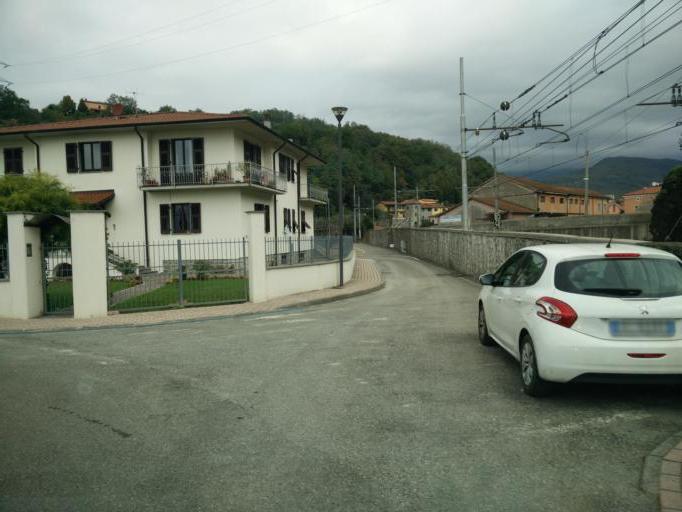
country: IT
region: Tuscany
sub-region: Provincia di Massa-Carrara
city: Pontremoli
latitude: 44.3797
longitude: 9.8841
